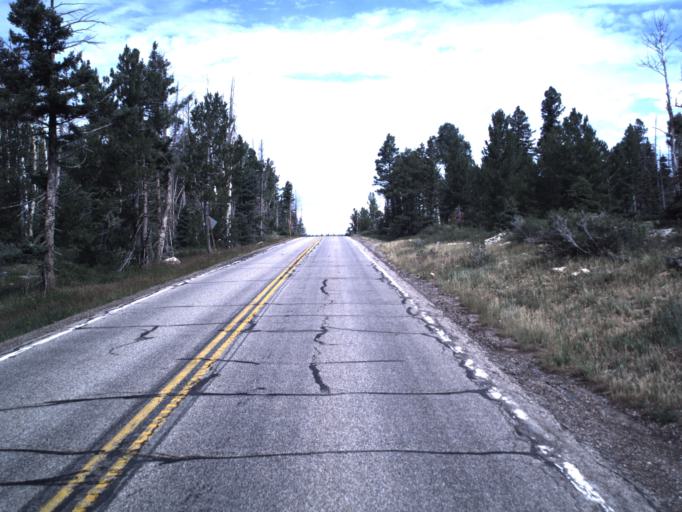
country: US
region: Utah
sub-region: Iron County
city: Parowan
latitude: 37.5287
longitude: -112.7639
